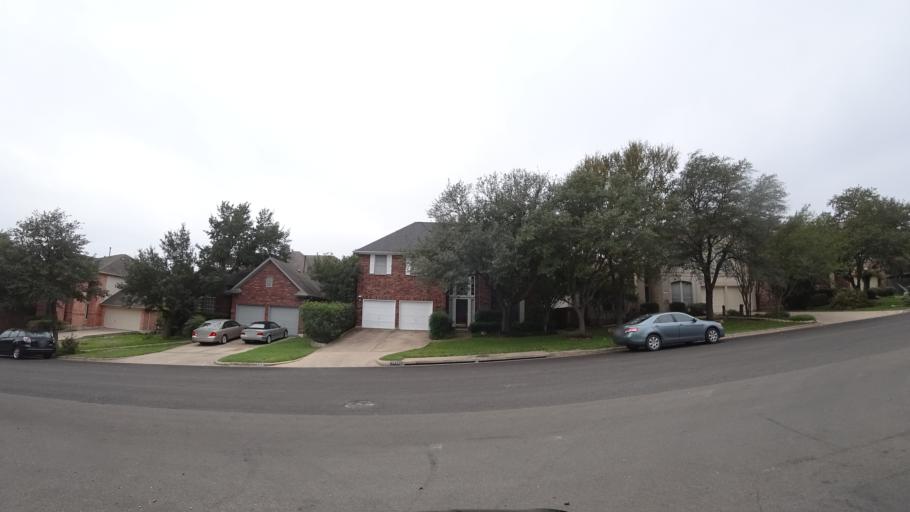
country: US
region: Texas
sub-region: Travis County
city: Shady Hollow
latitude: 30.1854
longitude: -97.8899
